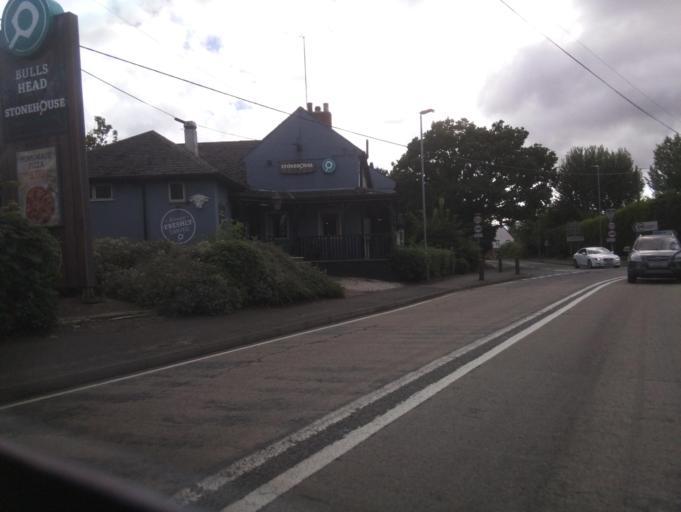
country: GB
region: England
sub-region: Leicestershire
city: Coalville
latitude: 52.7592
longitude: -1.3628
